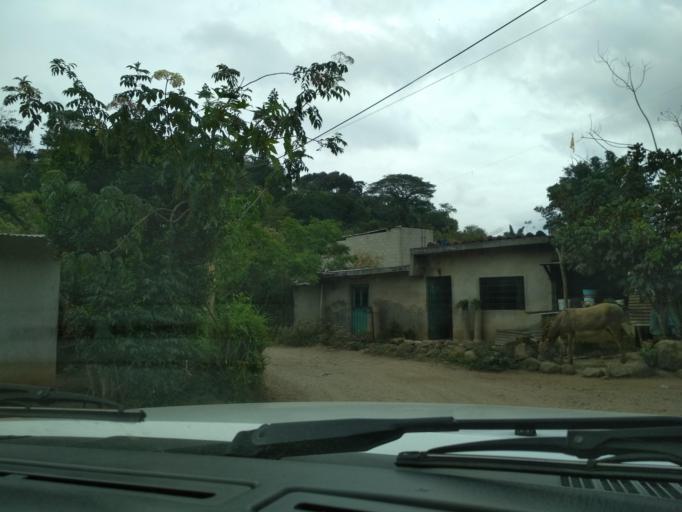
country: MX
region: Veracruz
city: El Castillo
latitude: 19.5797
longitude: -96.8648
